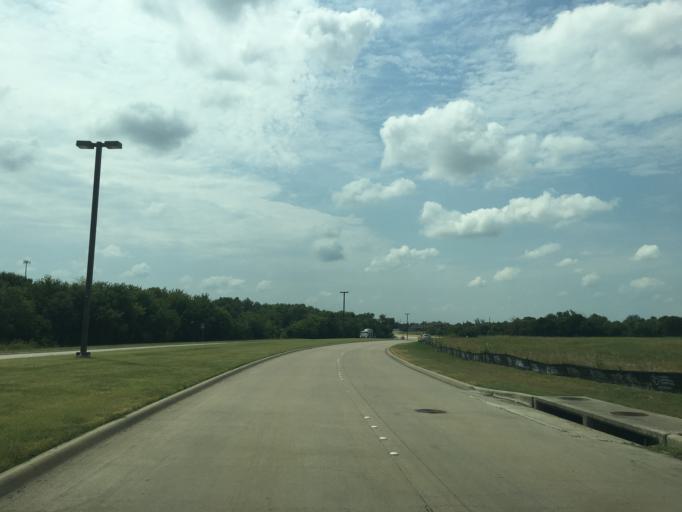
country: US
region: Texas
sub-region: Rockwall County
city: Rockwall
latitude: 32.9541
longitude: -96.4436
